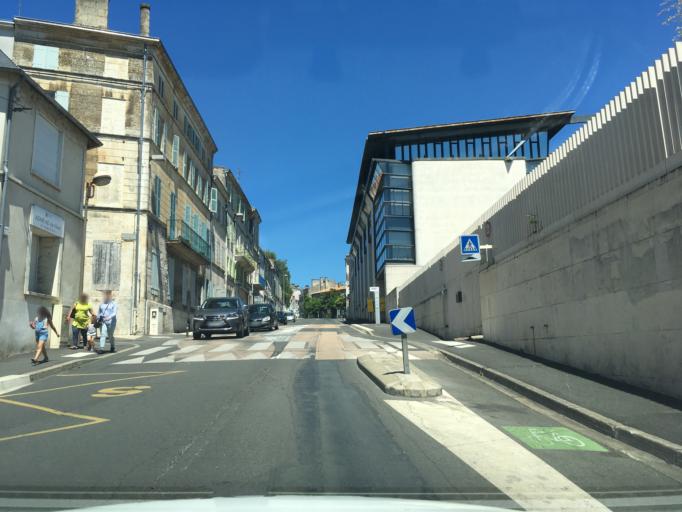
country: FR
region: Poitou-Charentes
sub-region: Departement des Deux-Sevres
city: Niort
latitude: 46.3280
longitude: -0.4580
